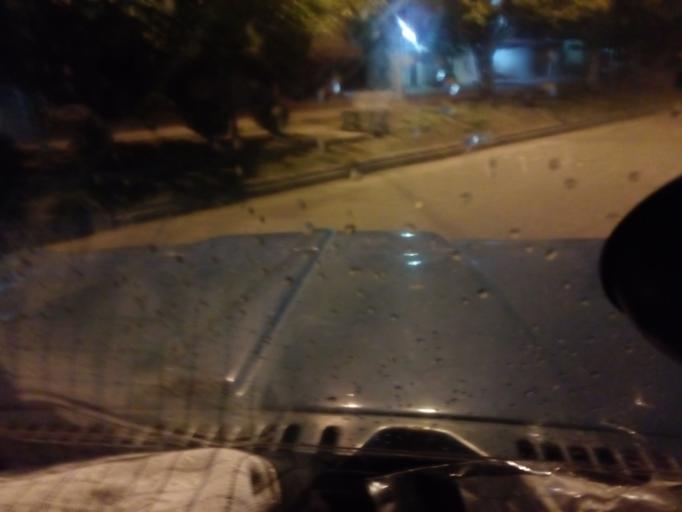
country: CO
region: Boyaca
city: Puerto Boyaca
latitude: 5.9752
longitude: -74.5871
